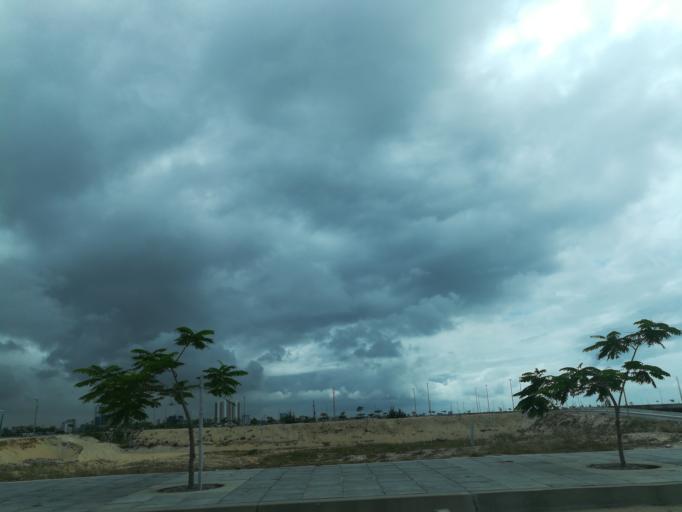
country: NG
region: Lagos
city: Ikoyi
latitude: 6.4135
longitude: 3.4140
